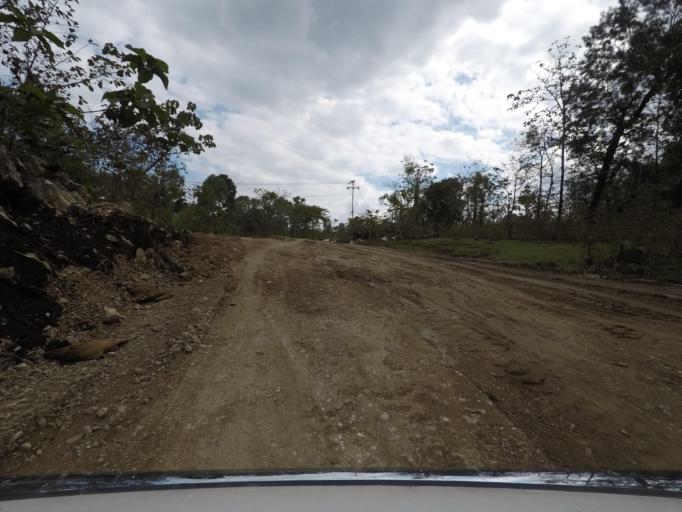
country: TL
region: Viqueque
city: Viqueque
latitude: -8.7735
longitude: 126.3774
